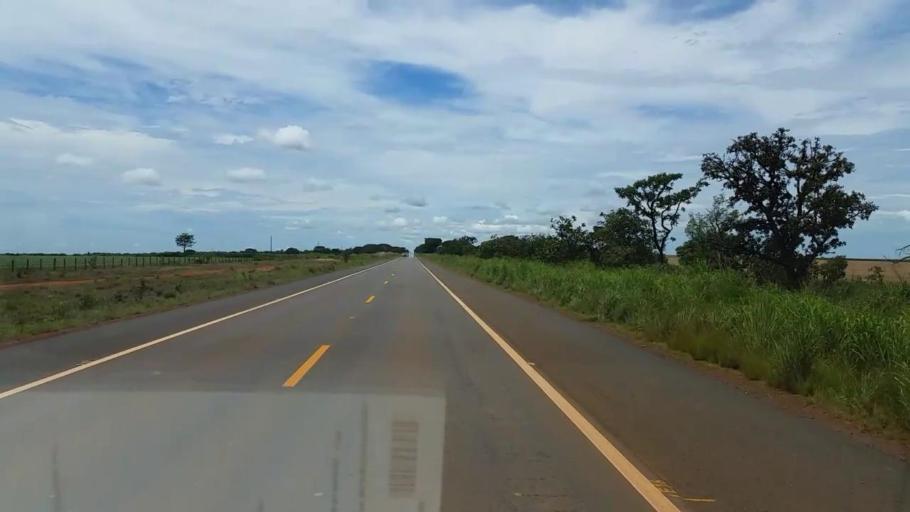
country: BR
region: Goias
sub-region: Luziania
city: Luziania
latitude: -16.2003
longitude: -47.4460
